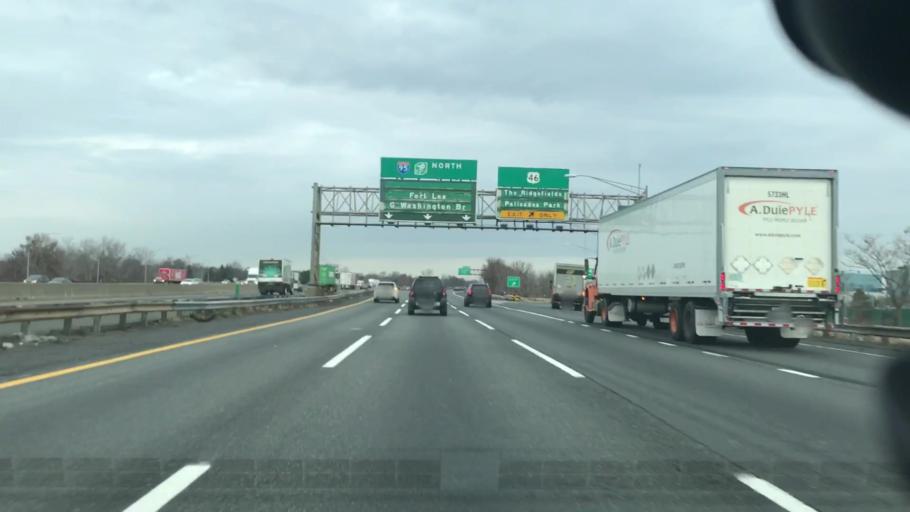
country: US
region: New Jersey
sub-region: Bergen County
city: Ridgefield
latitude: 40.8422
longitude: -74.0175
